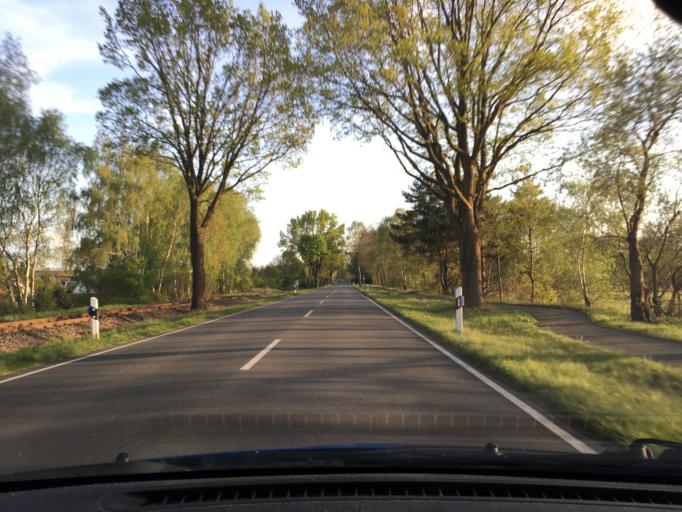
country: DE
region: Lower Saxony
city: Toppenstedt
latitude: 53.2701
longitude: 10.1206
